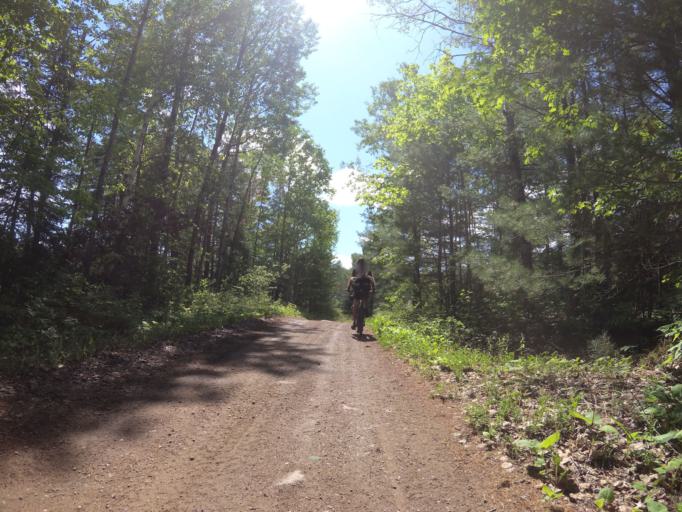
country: CA
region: Ontario
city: Renfrew
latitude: 45.1154
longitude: -76.8671
